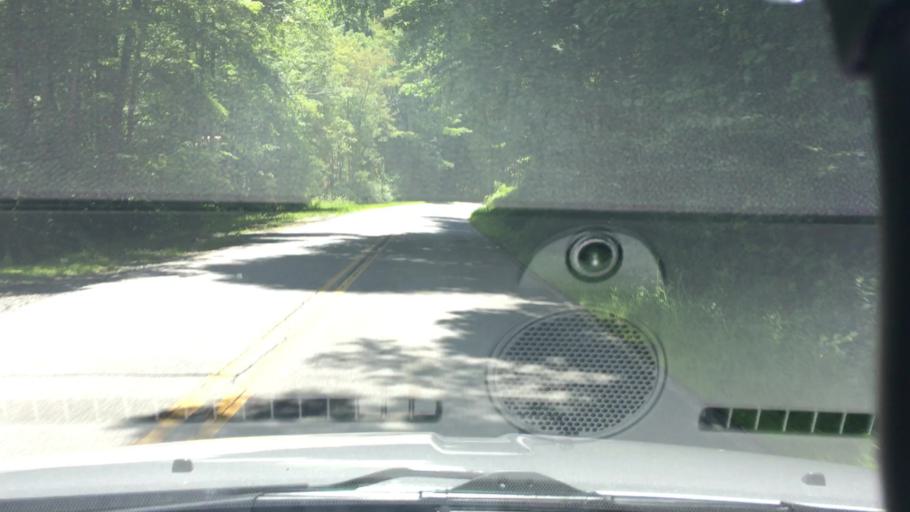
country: US
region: North Carolina
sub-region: Madison County
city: Mars Hill
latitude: 35.9208
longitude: -82.5314
